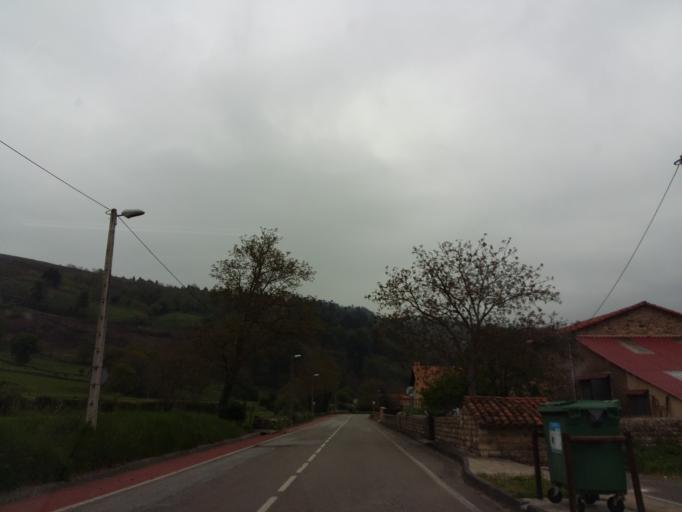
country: ES
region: Cantabria
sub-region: Provincia de Cantabria
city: Arenas de Iguna
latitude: 43.1944
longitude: -4.0642
